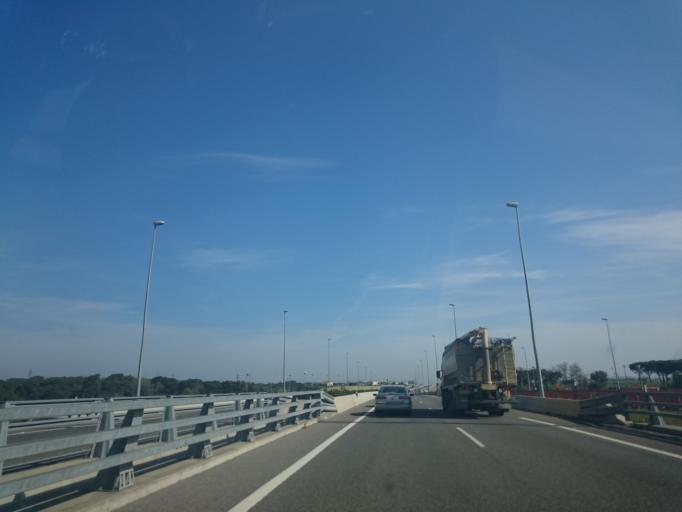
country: ES
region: Catalonia
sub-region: Provincia de Girona
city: Riudellots de la Selva
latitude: 41.8901
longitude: 2.7833
